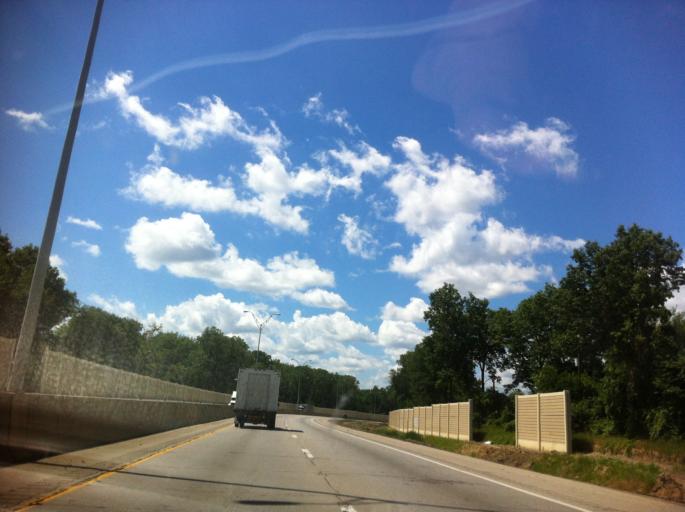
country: US
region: Ohio
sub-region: Lucas County
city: Ottawa Hills
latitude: 41.6879
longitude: -83.6519
